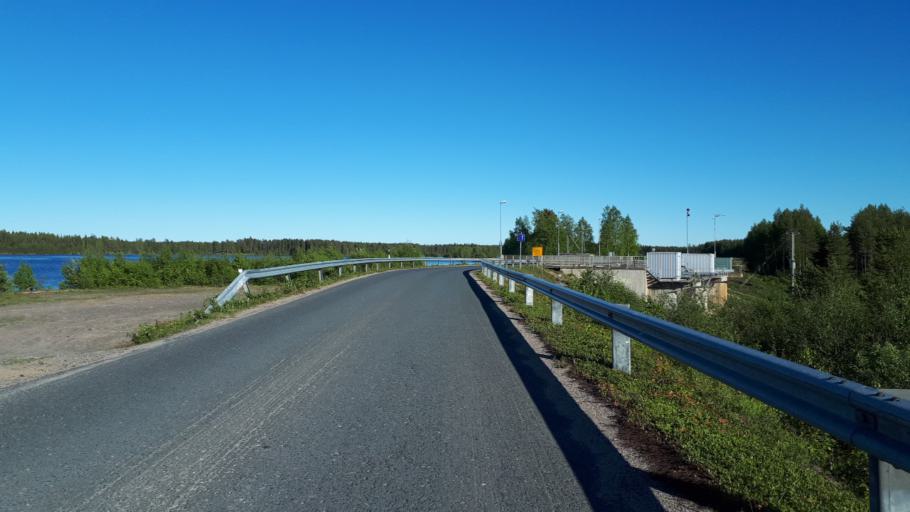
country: FI
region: Northern Ostrobothnia
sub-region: Oulunkaari
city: Ii
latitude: 65.3256
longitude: 25.5230
